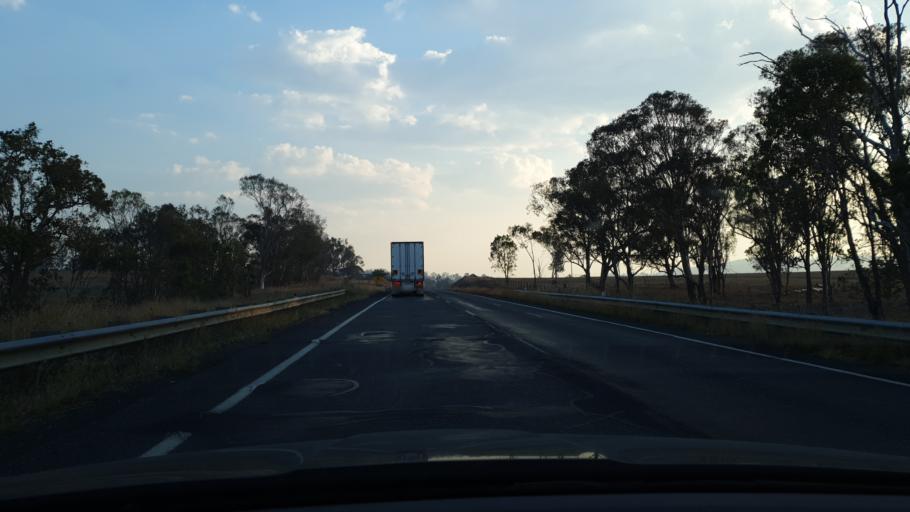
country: AU
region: New South Wales
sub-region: Tenterfield Municipality
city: Carrolls Creek
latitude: -29.1015
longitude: 152.0011
